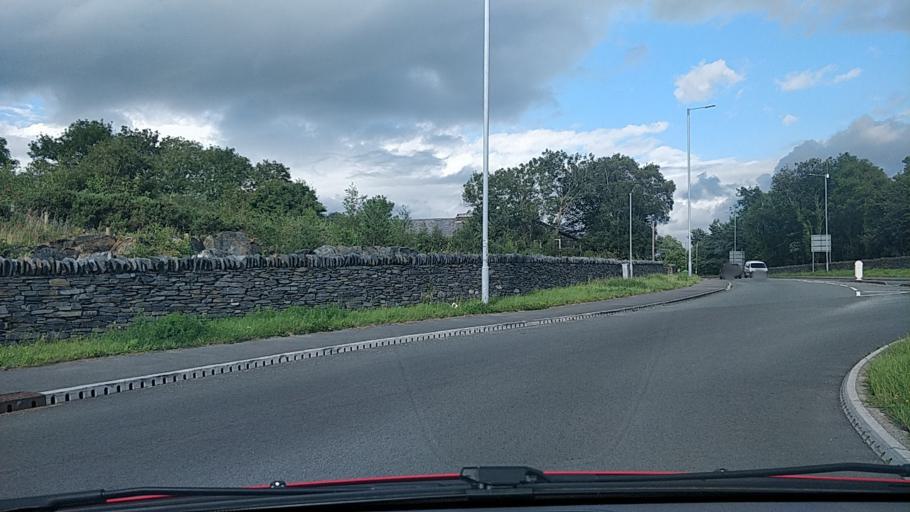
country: GB
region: Wales
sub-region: Gwynedd
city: Penrhyndeudraeth
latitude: 52.9266
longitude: -4.0812
